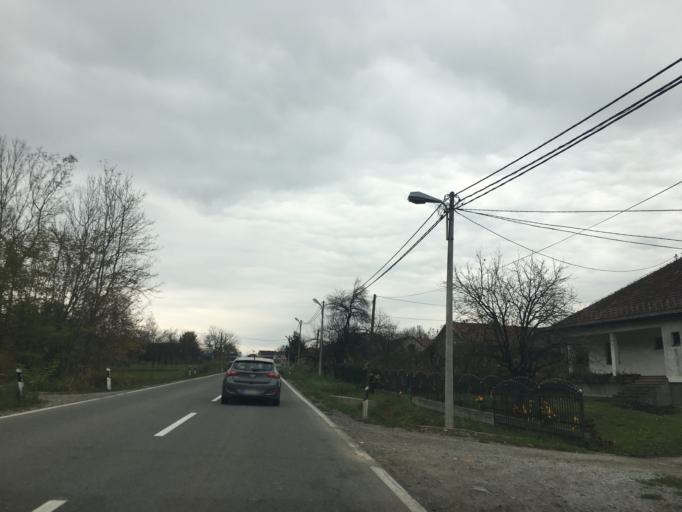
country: RS
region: Central Serbia
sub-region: Raski Okrug
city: Kraljevo
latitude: 43.7137
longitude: 20.7937
